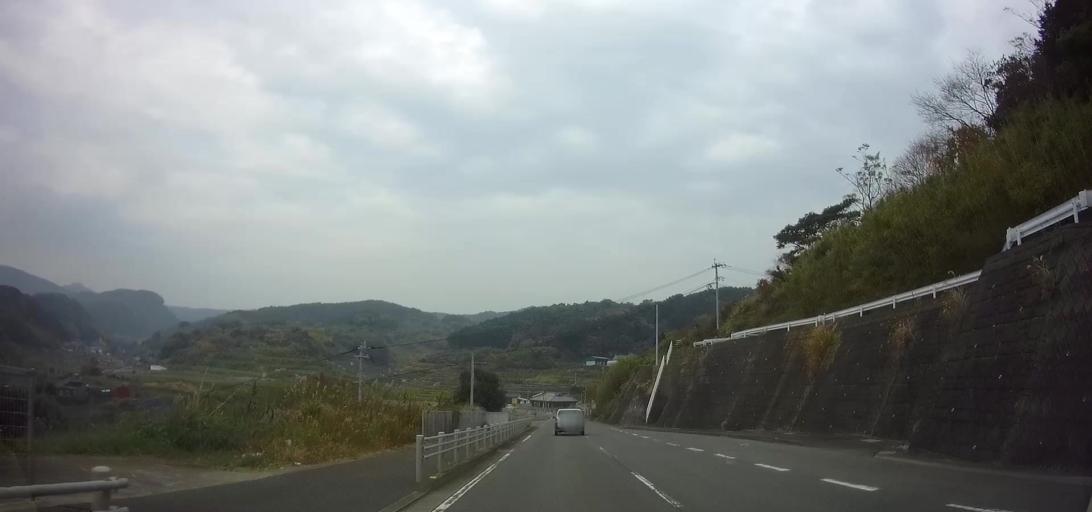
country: JP
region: Nagasaki
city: Shimabara
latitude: 32.7055
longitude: 130.1865
